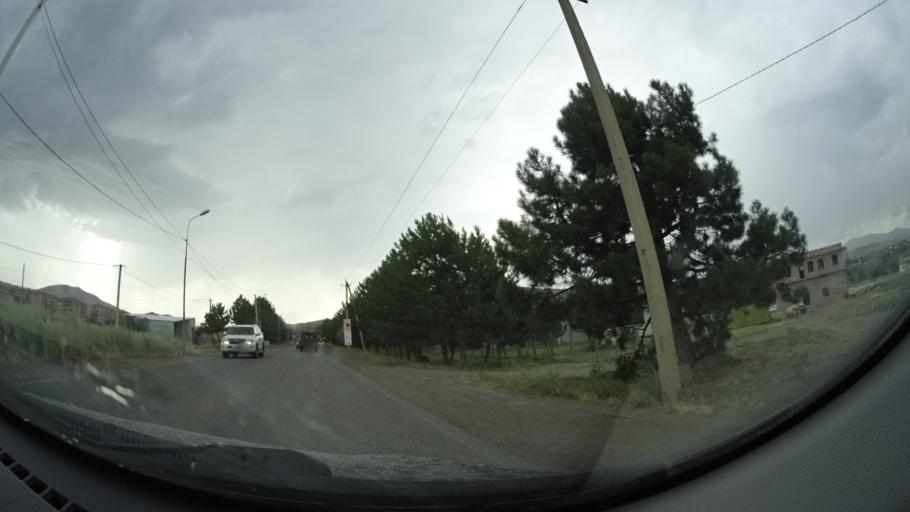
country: GE
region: Samtskhe-Javakheti
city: Akhaltsikhe
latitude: 41.6431
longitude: 43.0079
